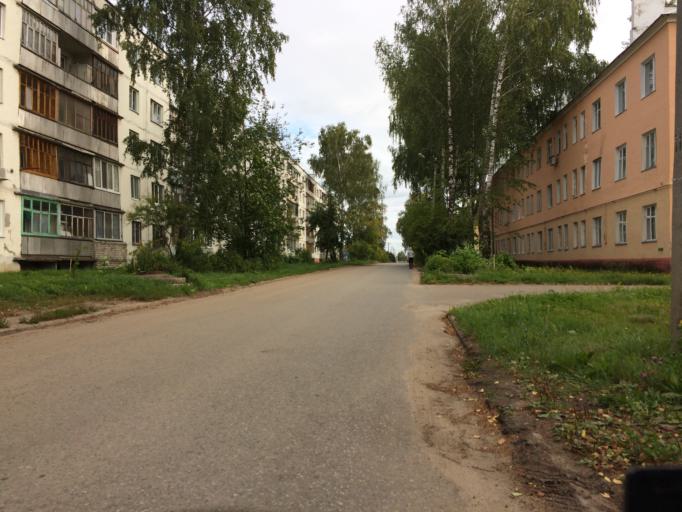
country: RU
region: Mariy-El
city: Yoshkar-Ola
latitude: 56.6574
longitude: 47.9795
